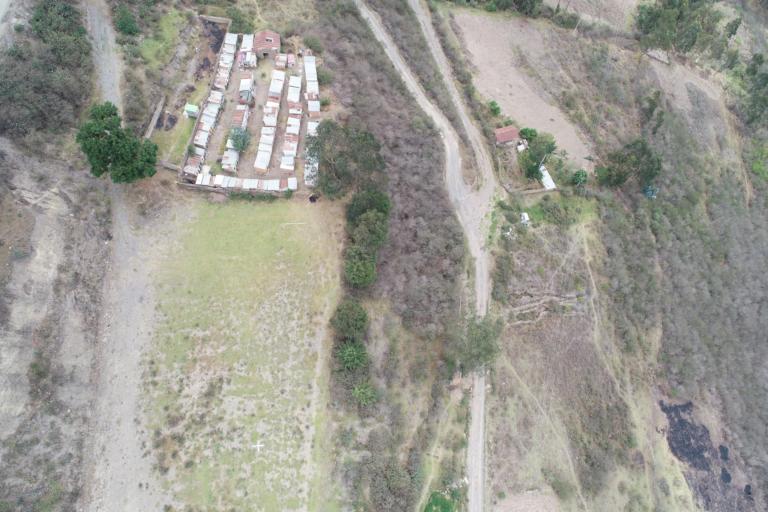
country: BO
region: La Paz
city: Sorata
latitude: -15.6388
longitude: -68.7040
